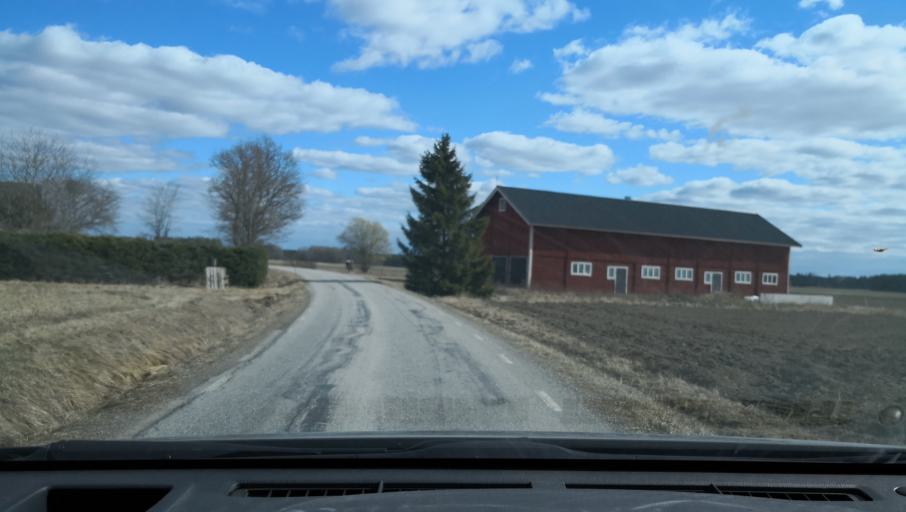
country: SE
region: Vaestmanland
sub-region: Sala Kommun
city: Sala
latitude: 59.8591
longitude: 16.6046
